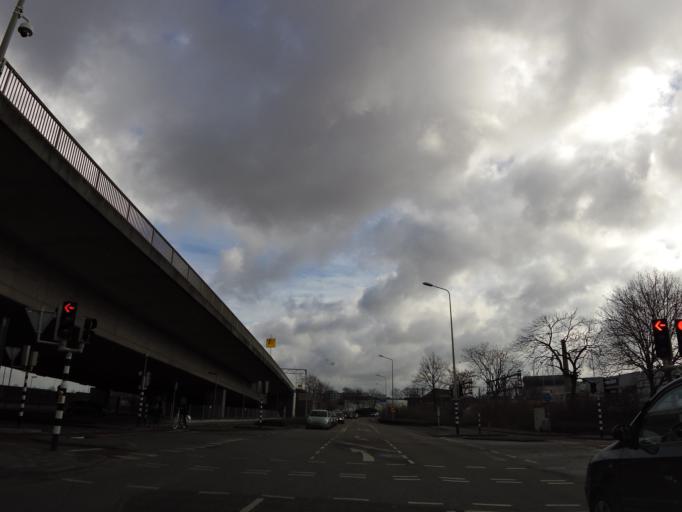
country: NL
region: Limburg
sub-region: Gemeente Maastricht
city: Maastricht
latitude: 50.8599
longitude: 5.7000
